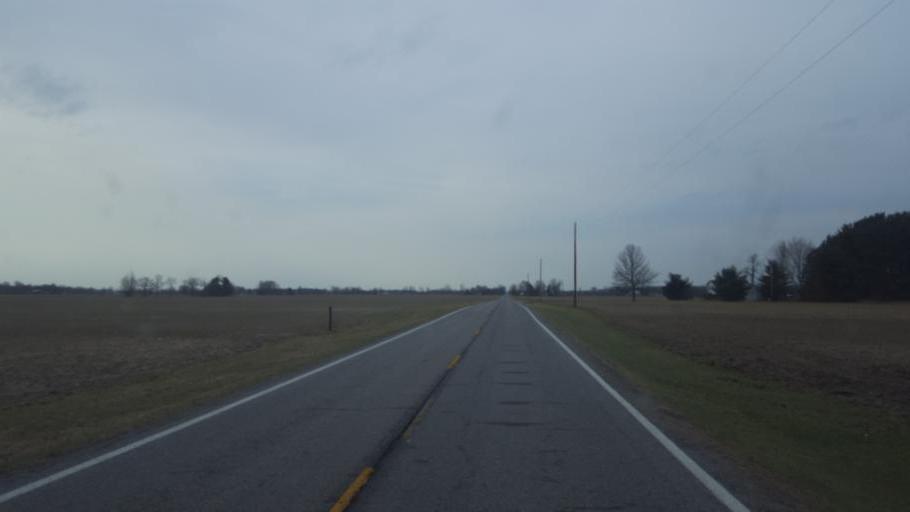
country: US
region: Ohio
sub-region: Morrow County
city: Cardington
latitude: 40.6130
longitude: -82.9624
